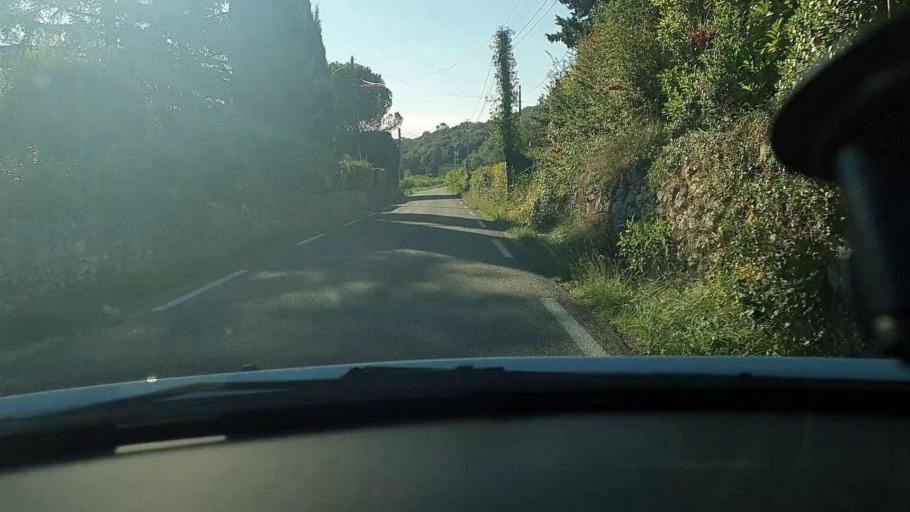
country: FR
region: Languedoc-Roussillon
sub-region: Departement du Gard
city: Goudargues
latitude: 44.2296
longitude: 4.4467
